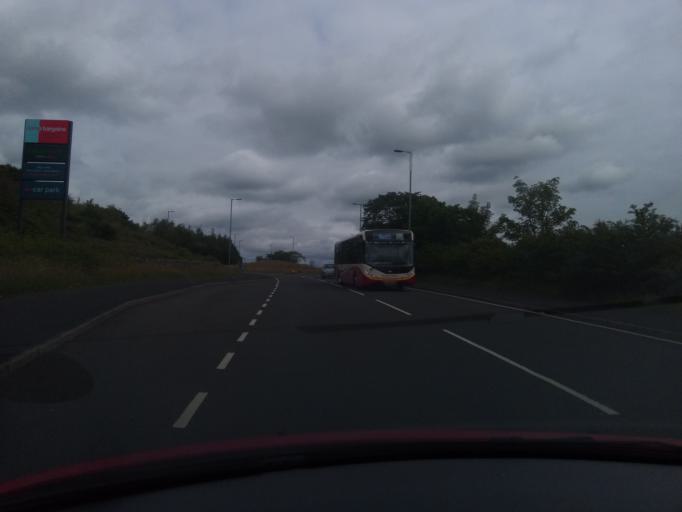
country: GB
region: Scotland
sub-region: The Scottish Borders
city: Hawick
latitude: 55.4411
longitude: -2.7756
